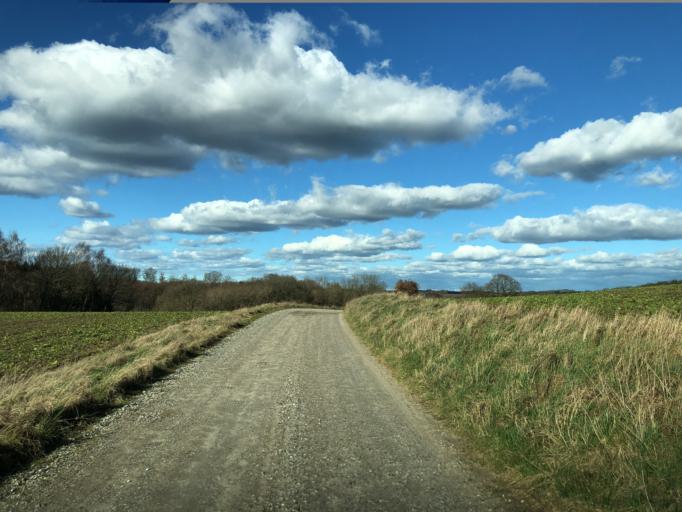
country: DK
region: Central Jutland
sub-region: Favrskov Kommune
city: Hammel
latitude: 56.3171
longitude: 9.9062
